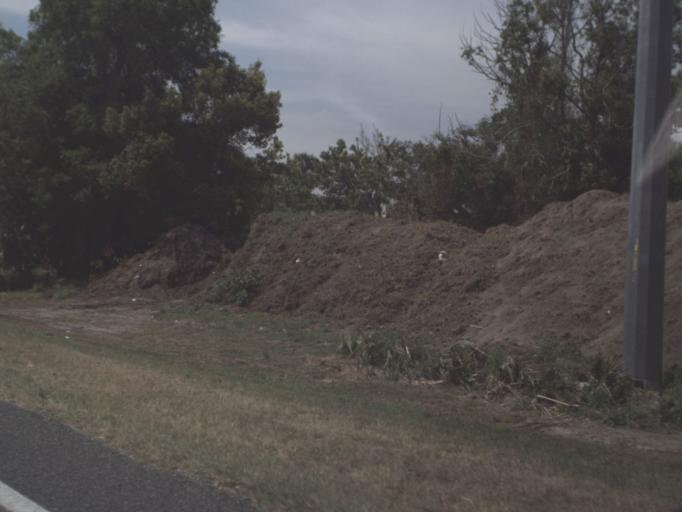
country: US
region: Florida
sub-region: Lake County
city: Umatilla
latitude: 28.9005
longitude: -81.6865
